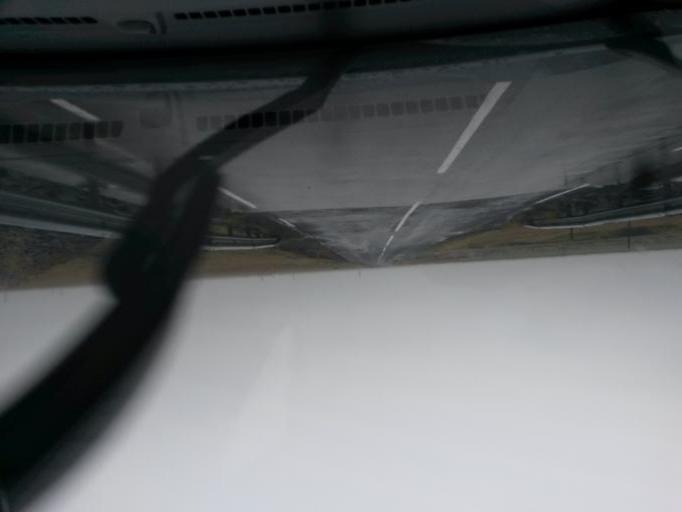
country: IS
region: South
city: Vestmannaeyjar
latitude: 63.5356
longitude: -19.6392
